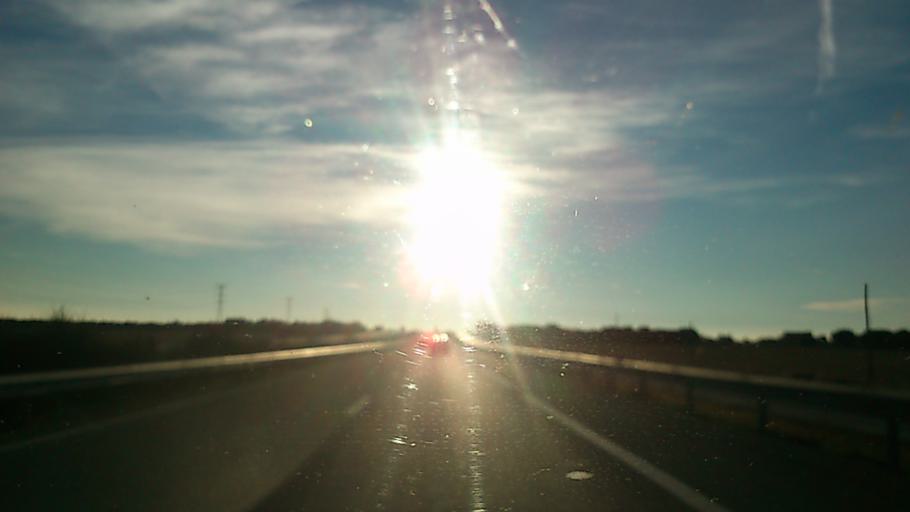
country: ES
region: Castille-La Mancha
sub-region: Provincia de Guadalajara
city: Gajanejos
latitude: 40.8328
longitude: -2.9061
